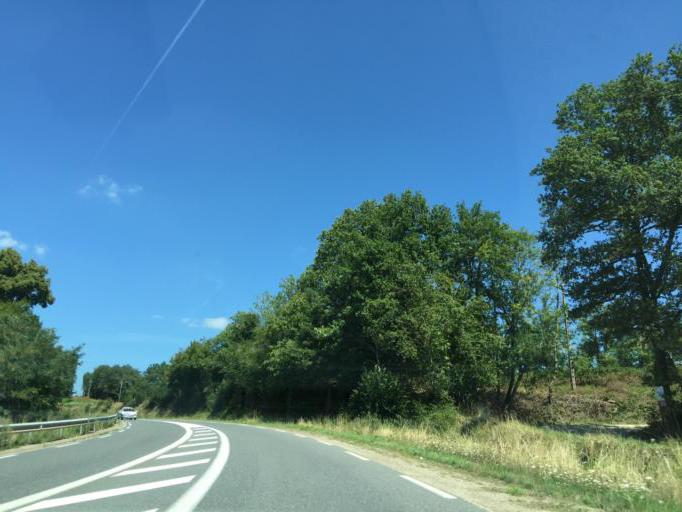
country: FR
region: Midi-Pyrenees
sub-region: Departement de l'Aveyron
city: Espalion
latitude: 44.5582
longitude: 2.7863
